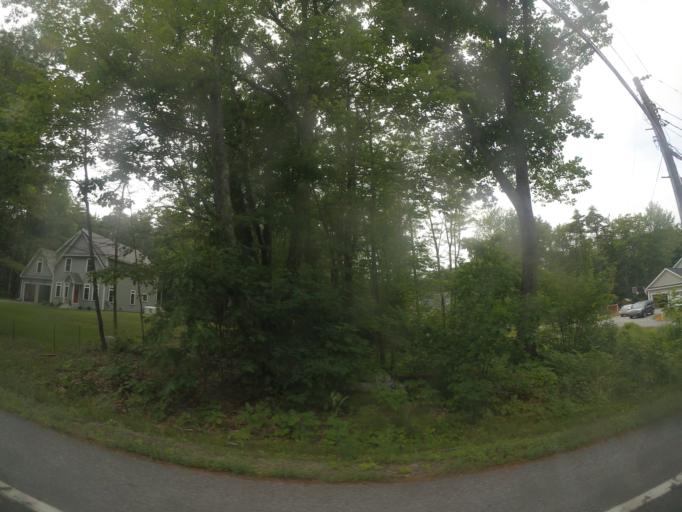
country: US
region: Maine
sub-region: Cumberland County
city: Falmouth
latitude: 43.7413
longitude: -70.2389
